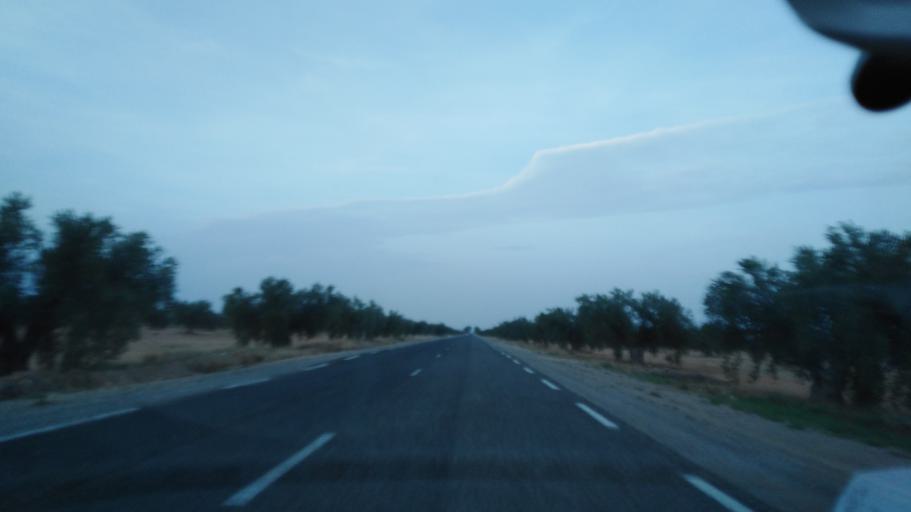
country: TN
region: Al Mahdiyah
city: Shurban
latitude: 34.9378
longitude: 10.3948
